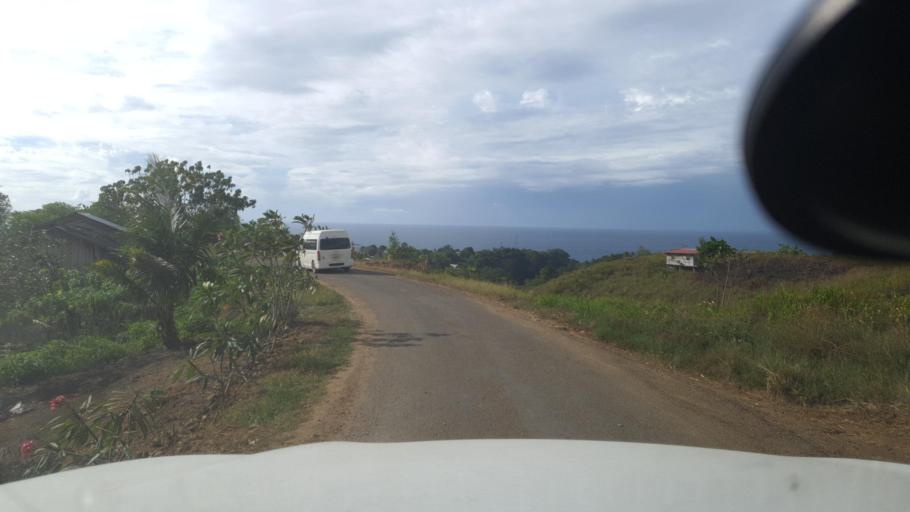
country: SB
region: Guadalcanal
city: Honiara
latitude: -9.4438
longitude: 159.9375
